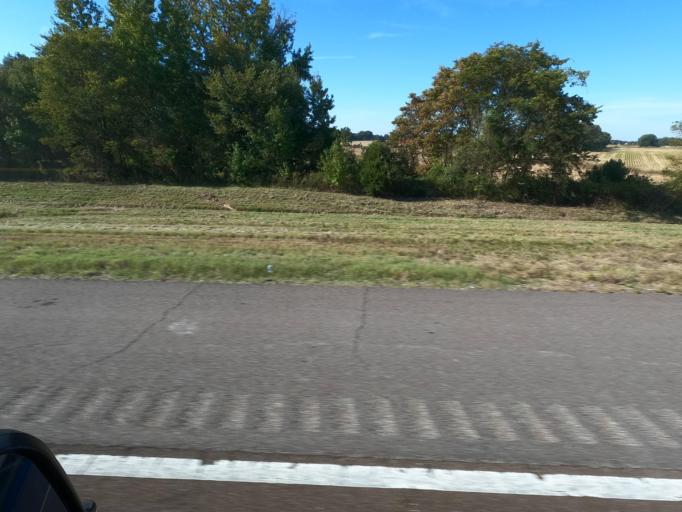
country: US
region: Tennessee
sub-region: Dyer County
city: Newbern
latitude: 36.1030
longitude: -89.3040
